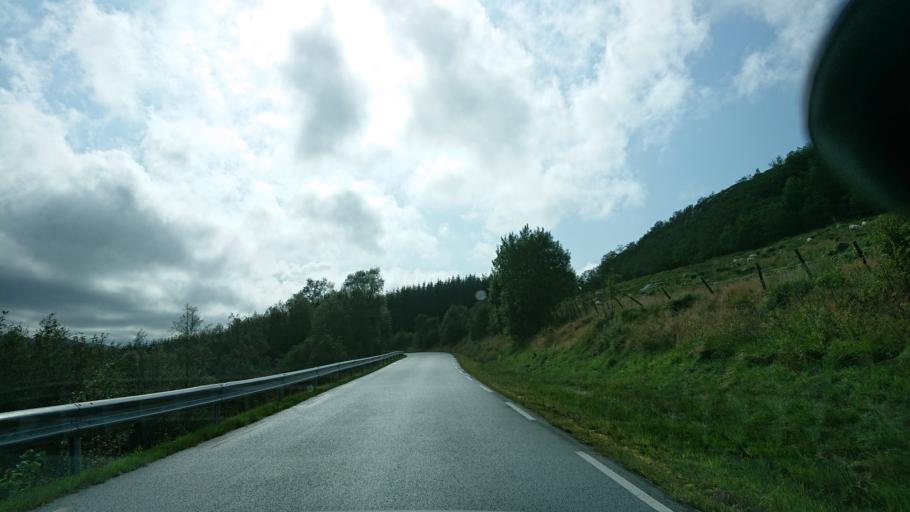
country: NO
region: Rogaland
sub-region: Gjesdal
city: Algard
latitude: 58.6907
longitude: 5.8787
